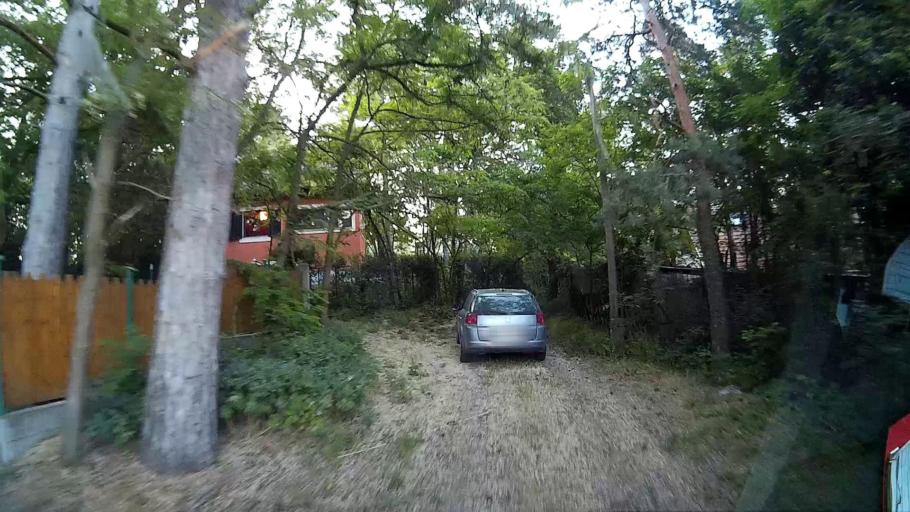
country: HU
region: Pest
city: Leanyfalu
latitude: 47.7028
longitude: 19.1083
